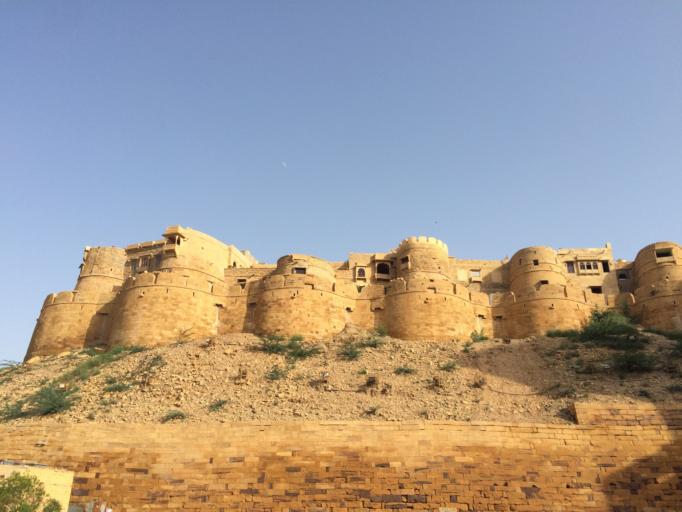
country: IN
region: Rajasthan
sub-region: Jaisalmer
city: Jaisalmer
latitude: 26.9133
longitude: 70.9138
